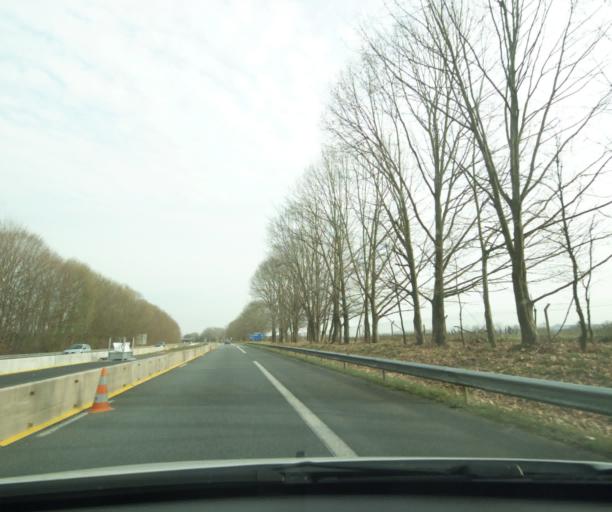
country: FR
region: Aquitaine
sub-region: Departement des Pyrenees-Atlantiques
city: Artix
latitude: 43.3888
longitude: -0.5370
